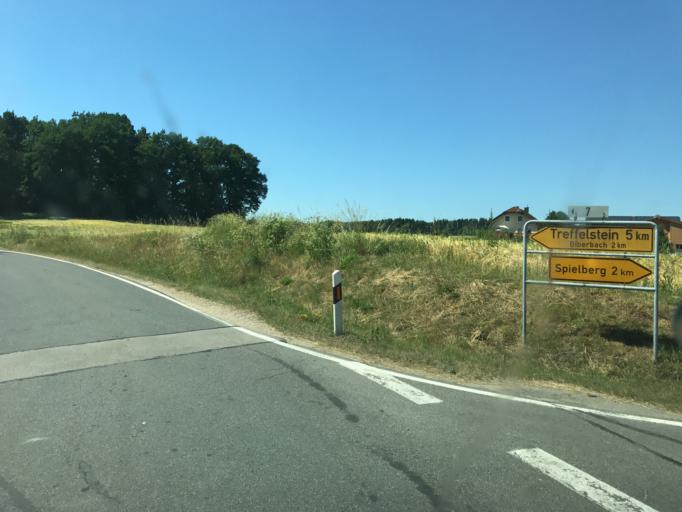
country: DE
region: Bavaria
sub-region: Upper Palatinate
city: Treffelstein
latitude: 49.3861
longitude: 12.6503
